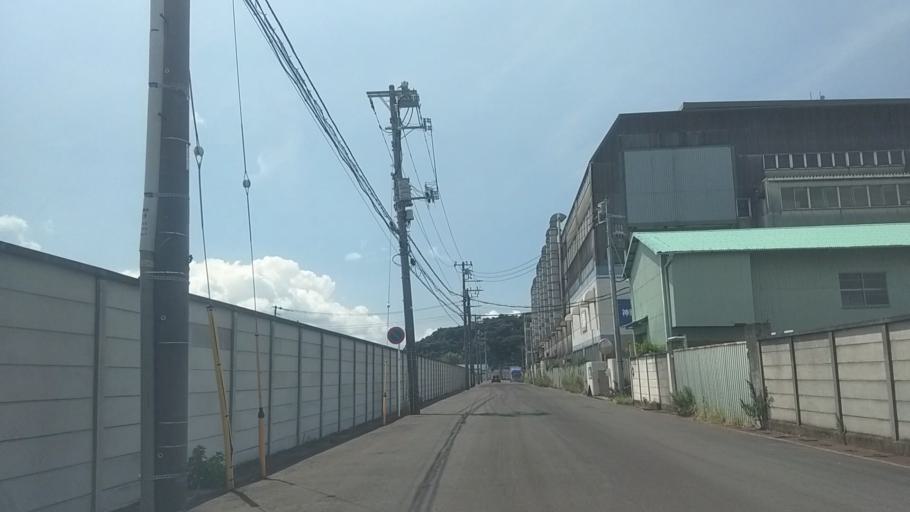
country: JP
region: Kanagawa
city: Yokosuka
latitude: 35.3098
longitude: 139.6423
